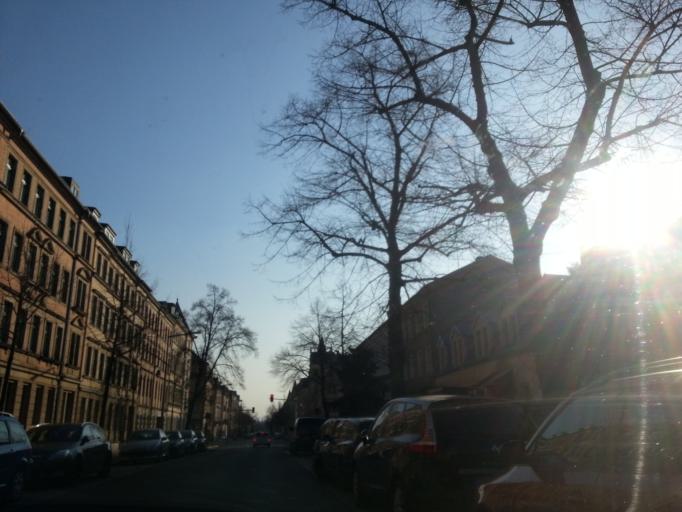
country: DE
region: Saxony
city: Albertstadt
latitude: 51.0899
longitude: 13.7312
